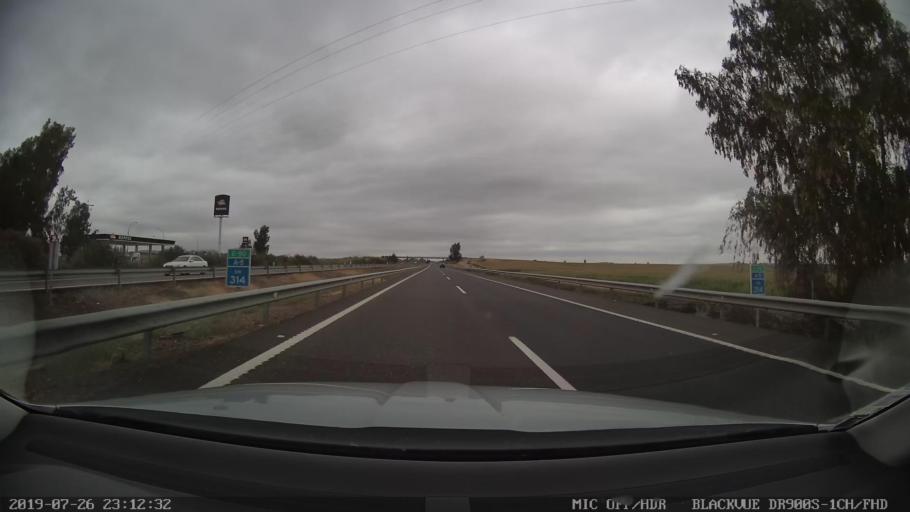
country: ES
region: Extremadura
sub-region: Provincia de Badajoz
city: Santa Amalia
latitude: 39.0052
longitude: -6.0907
